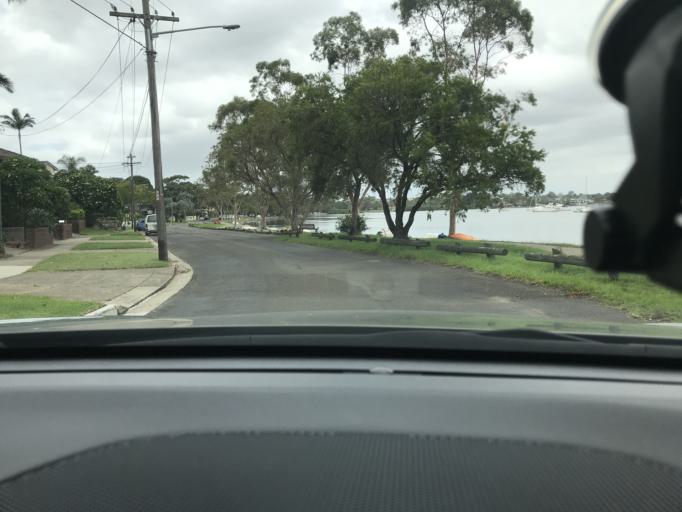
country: AU
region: New South Wales
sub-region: Canada Bay
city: Wareemba
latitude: -33.8540
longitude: 151.1262
